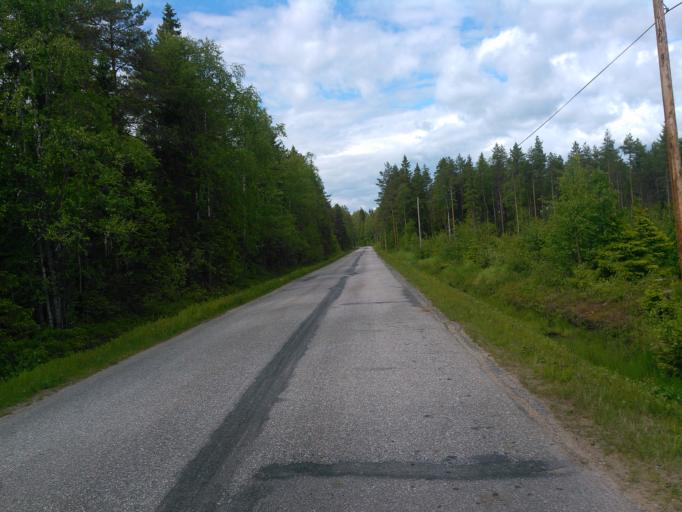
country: SE
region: Vaesterbotten
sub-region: Umea Kommun
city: Ersmark
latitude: 63.8737
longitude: 20.3280
